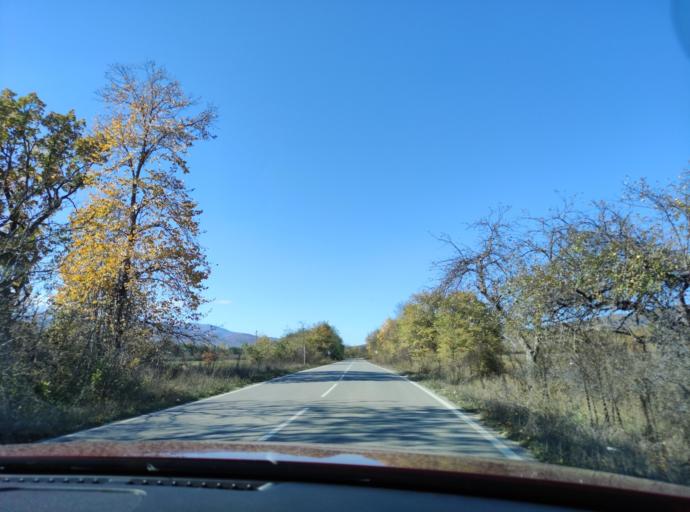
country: BG
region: Montana
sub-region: Obshtina Chiprovtsi
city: Chiprovtsi
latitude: 43.4190
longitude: 23.0240
